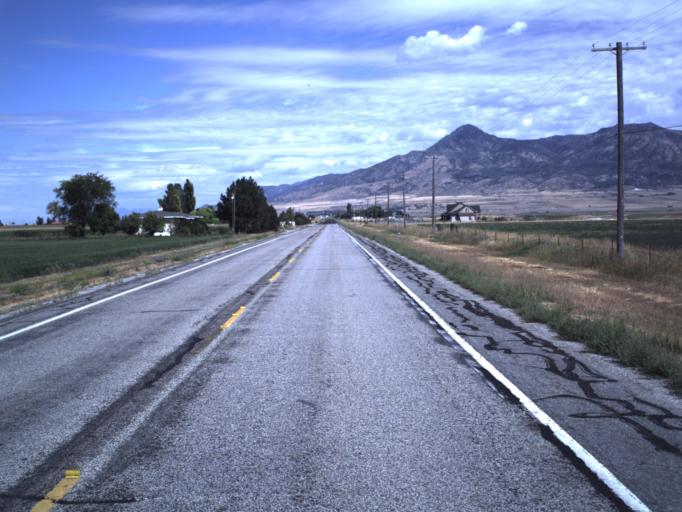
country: US
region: Utah
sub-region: Box Elder County
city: Garland
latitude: 41.8187
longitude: -112.1454
